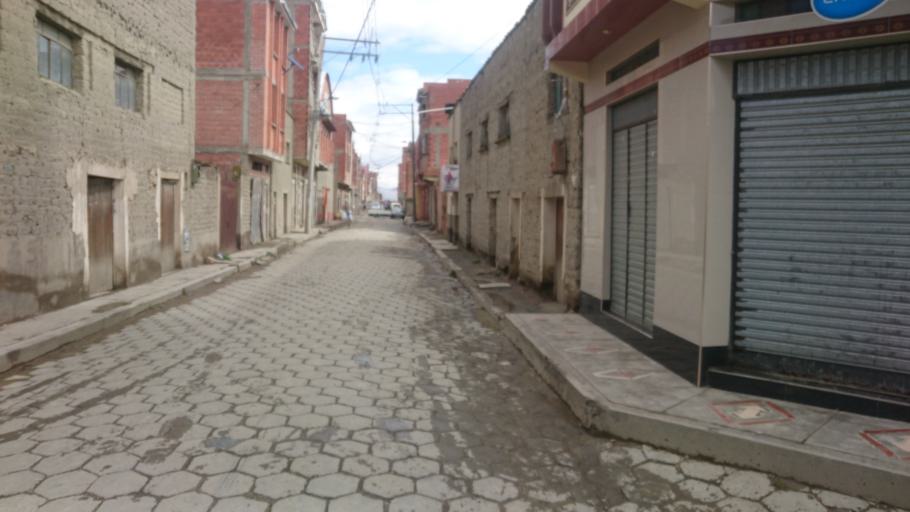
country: BO
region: La Paz
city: Achacachi
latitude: -16.0422
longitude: -68.6860
